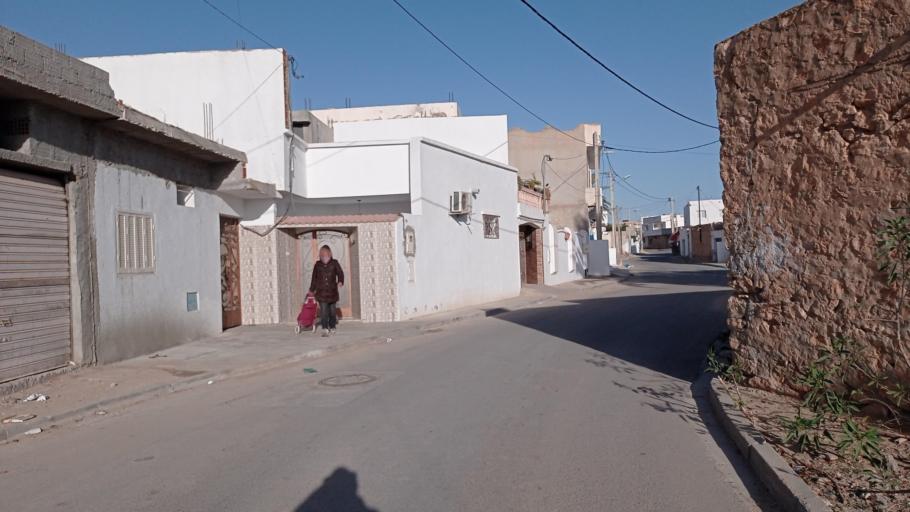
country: TN
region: Qabis
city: Gabes
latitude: 33.8557
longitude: 10.1192
